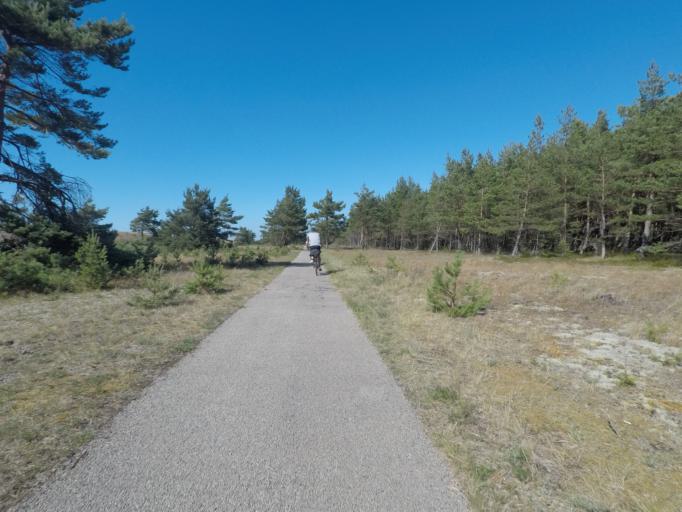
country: LT
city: Neringa
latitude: 55.4949
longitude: 21.0874
